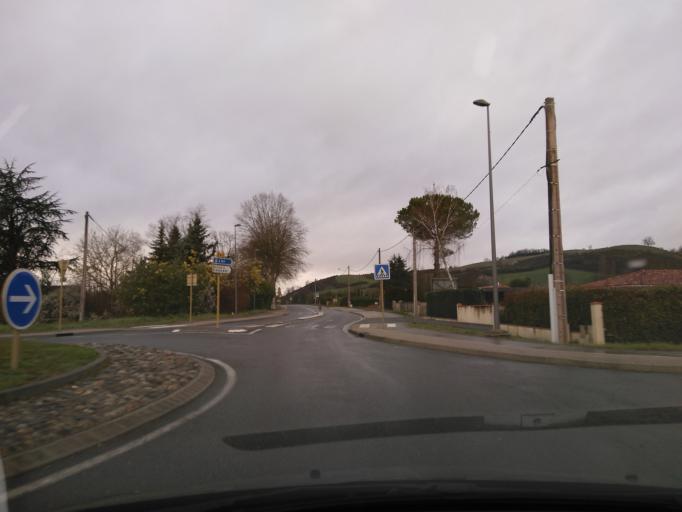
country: FR
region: Midi-Pyrenees
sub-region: Departement de la Haute-Garonne
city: Montesquieu-Volvestre
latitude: 43.2184
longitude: 1.2190
